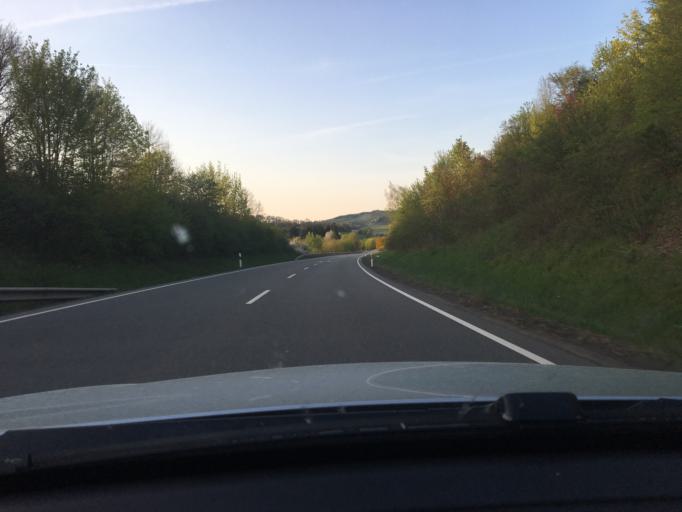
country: DE
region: Rheinland-Pfalz
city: Winnweiler
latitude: 49.5623
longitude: 7.8627
